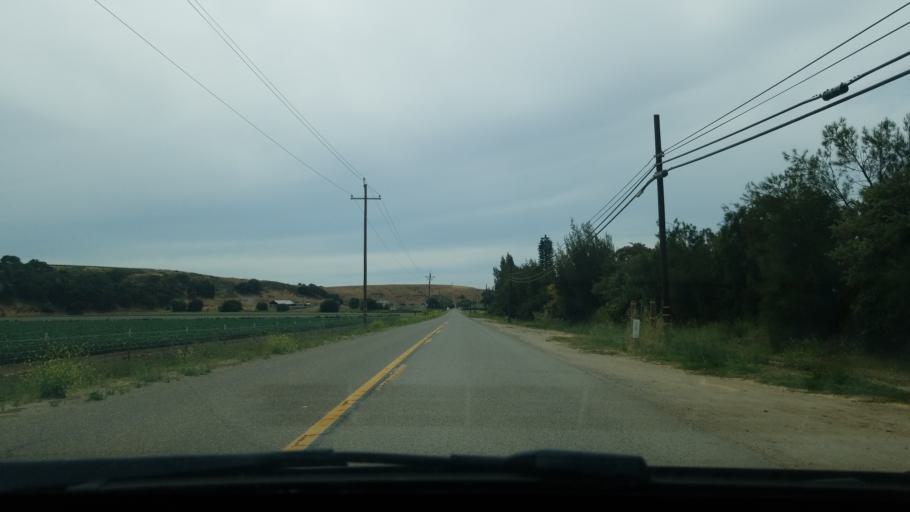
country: US
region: California
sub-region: Santa Barbara County
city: Los Alamos
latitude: 34.8645
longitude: -120.2834
